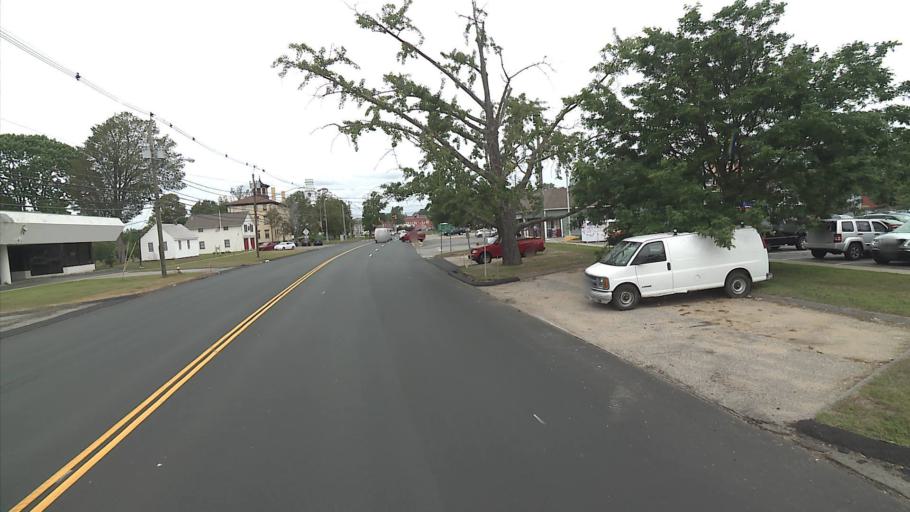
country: US
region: Connecticut
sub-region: New London County
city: Colchester
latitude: 41.5725
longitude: -72.3317
